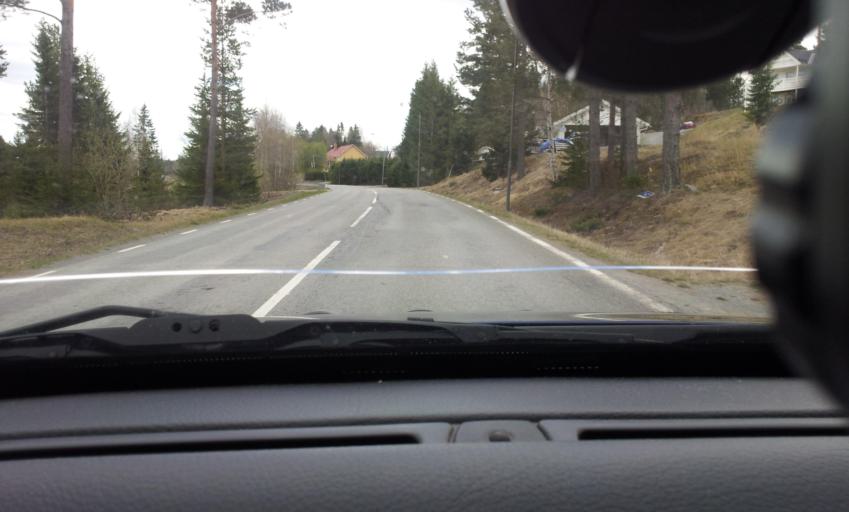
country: SE
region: Jaemtland
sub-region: OEstersunds Kommun
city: Ostersund
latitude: 63.1381
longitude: 14.6322
